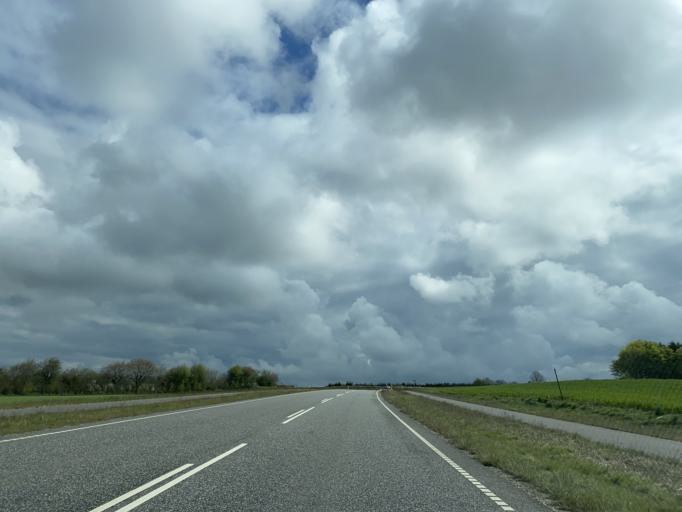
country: DK
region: Central Jutland
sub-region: Silkeborg Kommune
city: Silkeborg
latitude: 56.2103
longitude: 9.5153
